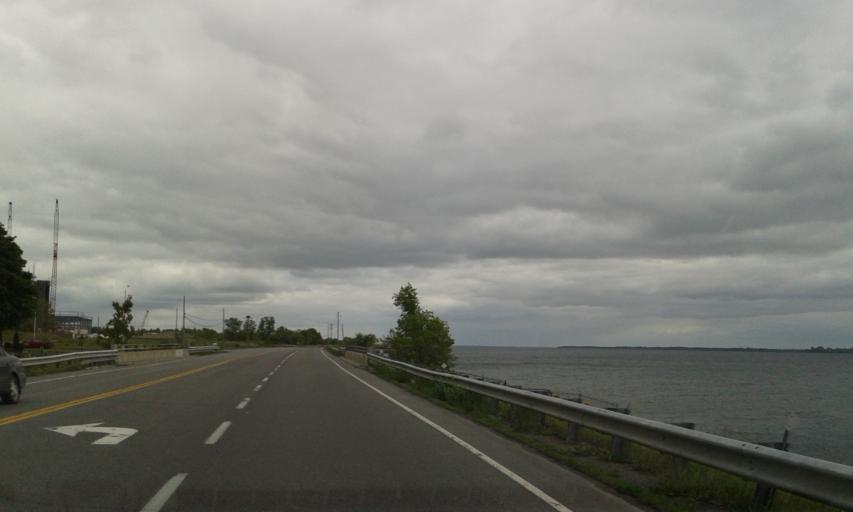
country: CA
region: Ontario
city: Skatepark
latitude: 44.1423
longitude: -76.8485
